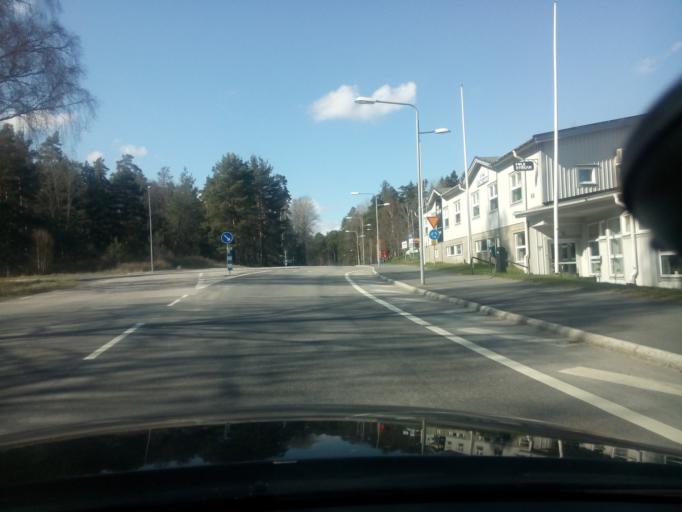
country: SE
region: Soedermanland
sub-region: Flens Kommun
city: Malmkoping
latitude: 59.1401
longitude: 16.7187
